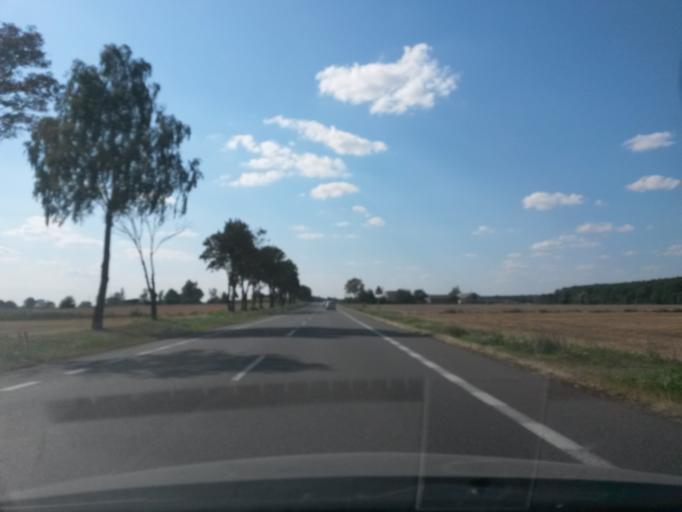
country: PL
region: Masovian Voivodeship
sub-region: Powiat plocki
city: Bulkowo
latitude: 52.6436
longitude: 20.1151
